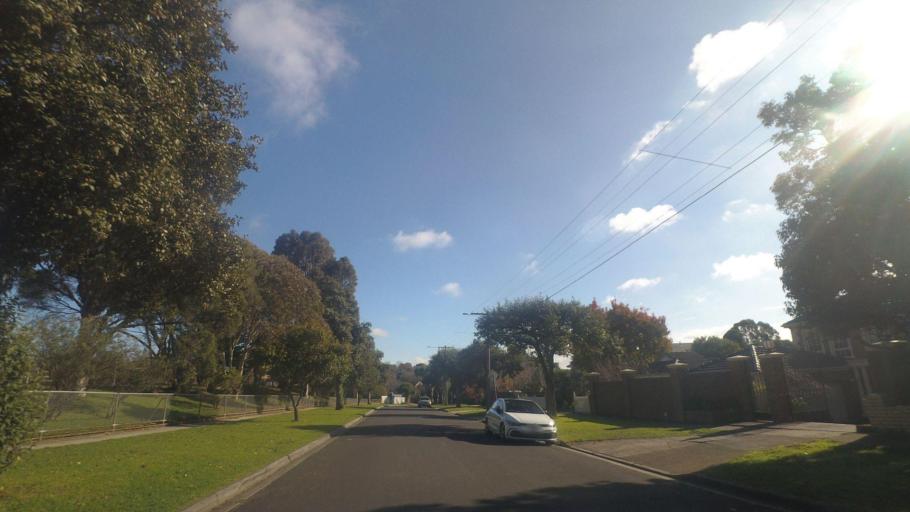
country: AU
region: Victoria
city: Mont Albert
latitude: -37.8110
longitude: 145.1043
